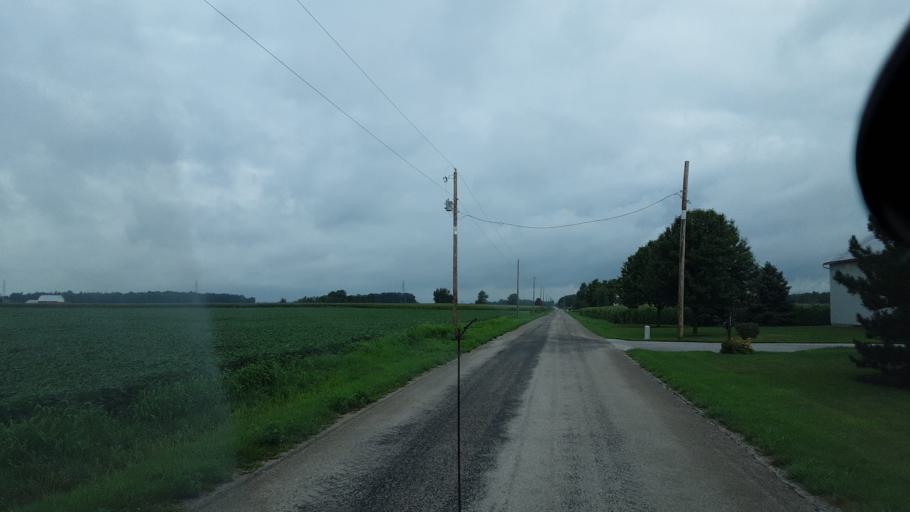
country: US
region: Indiana
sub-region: Allen County
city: Monroeville
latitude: 40.9153
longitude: -84.8427
